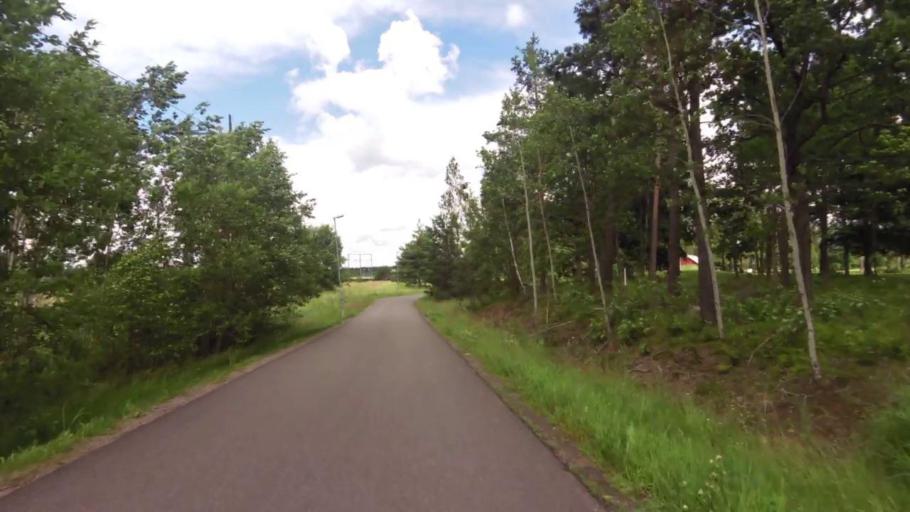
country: SE
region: OEstergoetland
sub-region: Linkopings Kommun
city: Malmslatt
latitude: 58.4019
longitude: 15.5555
